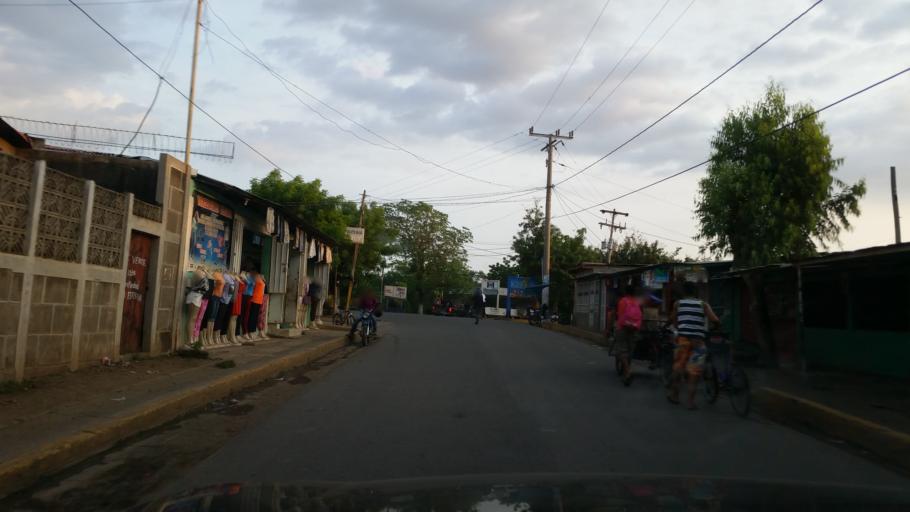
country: NI
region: Managua
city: Masachapa
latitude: 11.7817
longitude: -86.5150
